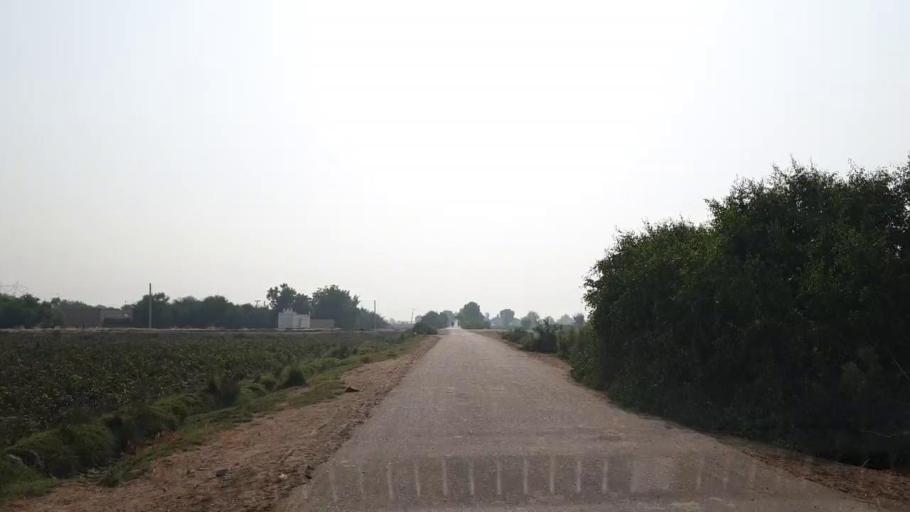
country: PK
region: Sindh
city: Bhan
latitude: 26.4799
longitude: 67.7707
